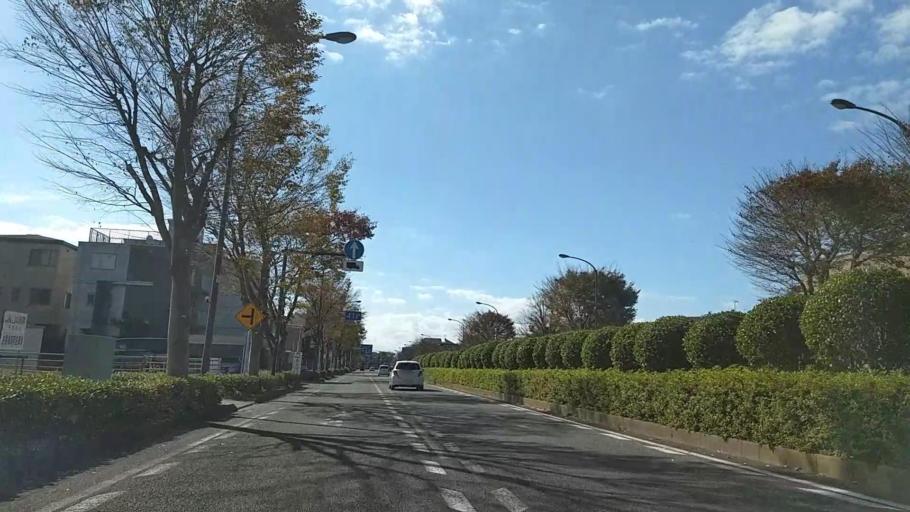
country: JP
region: Kanagawa
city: Hiratsuka
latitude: 35.3280
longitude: 139.3335
